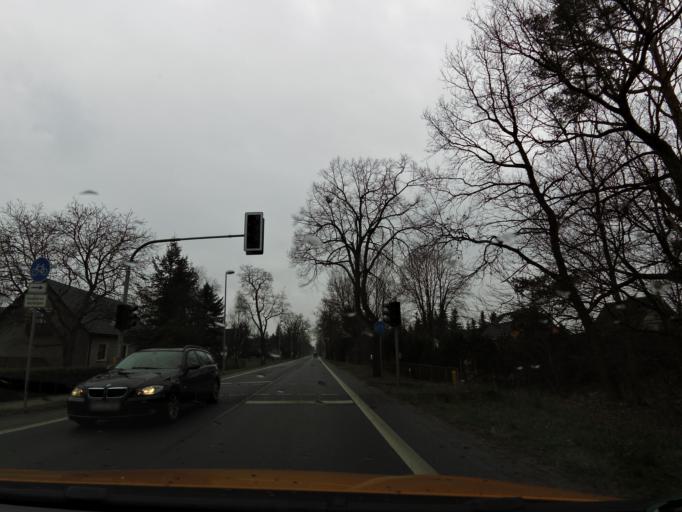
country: DE
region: Brandenburg
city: Gross Kreutz
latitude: 52.4067
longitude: 12.7408
